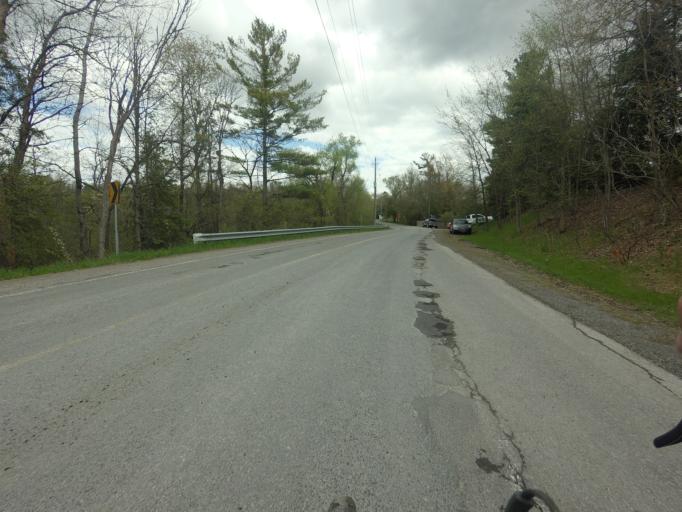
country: CA
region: Ontario
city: Carleton Place
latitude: 45.2666
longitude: -76.2487
